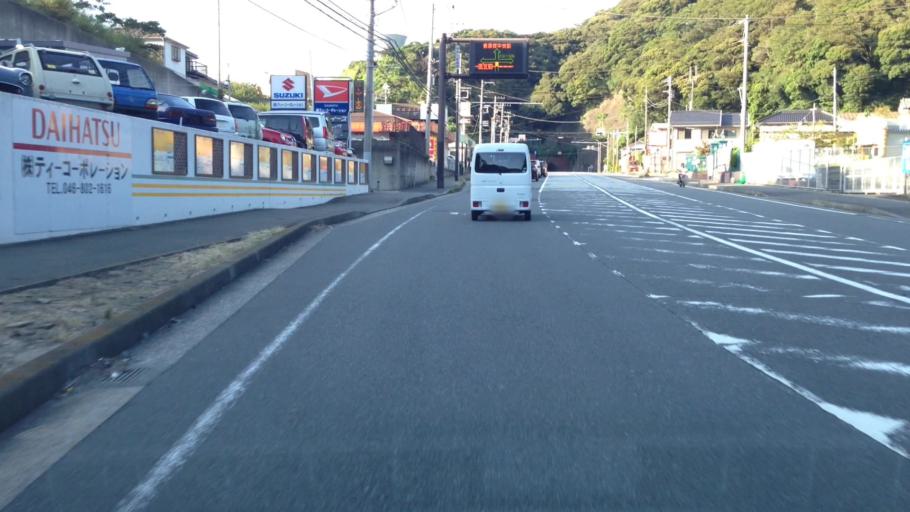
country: JP
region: Kanagawa
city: Yokosuka
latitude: 35.2315
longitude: 139.6568
